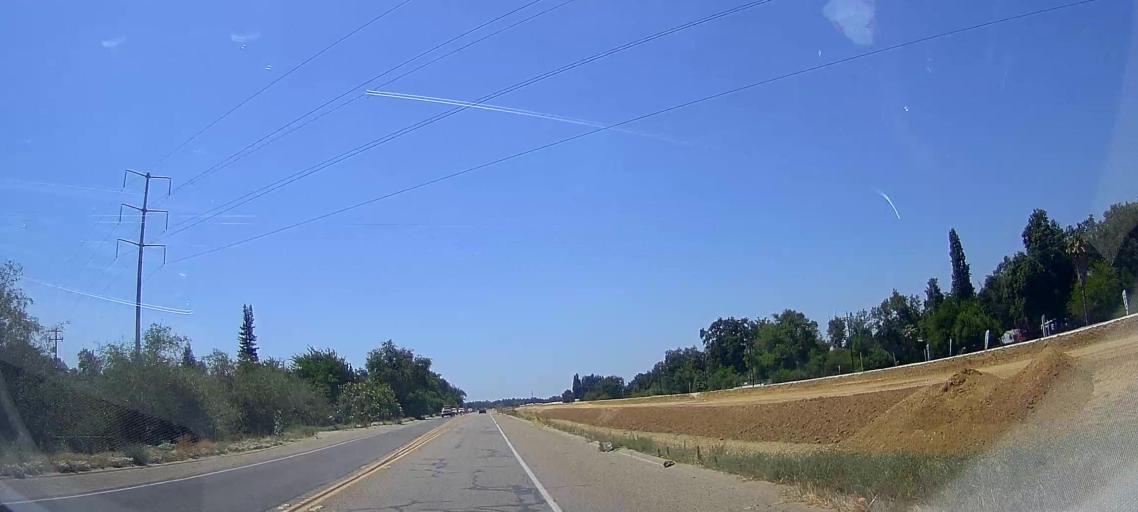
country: US
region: California
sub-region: Fresno County
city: Minkler
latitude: 36.7300
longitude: -119.4686
